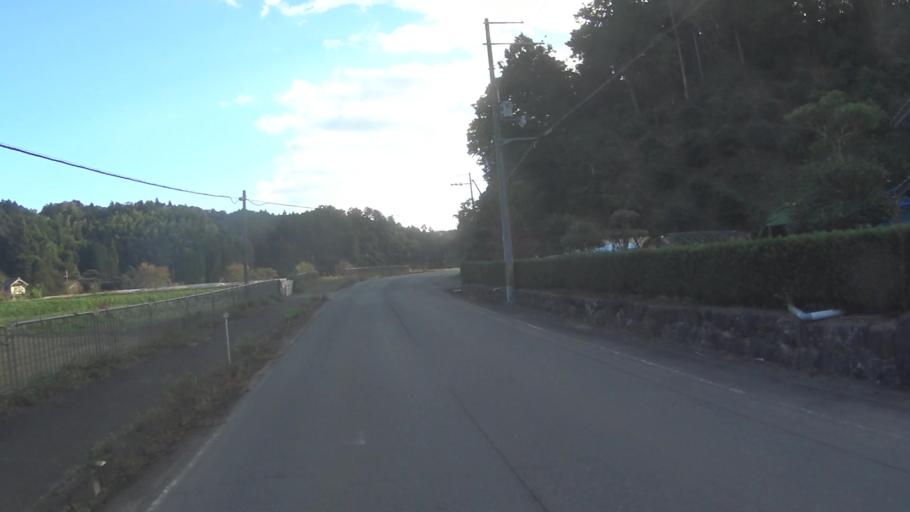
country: JP
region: Kyoto
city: Miyazu
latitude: 35.4528
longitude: 135.2169
